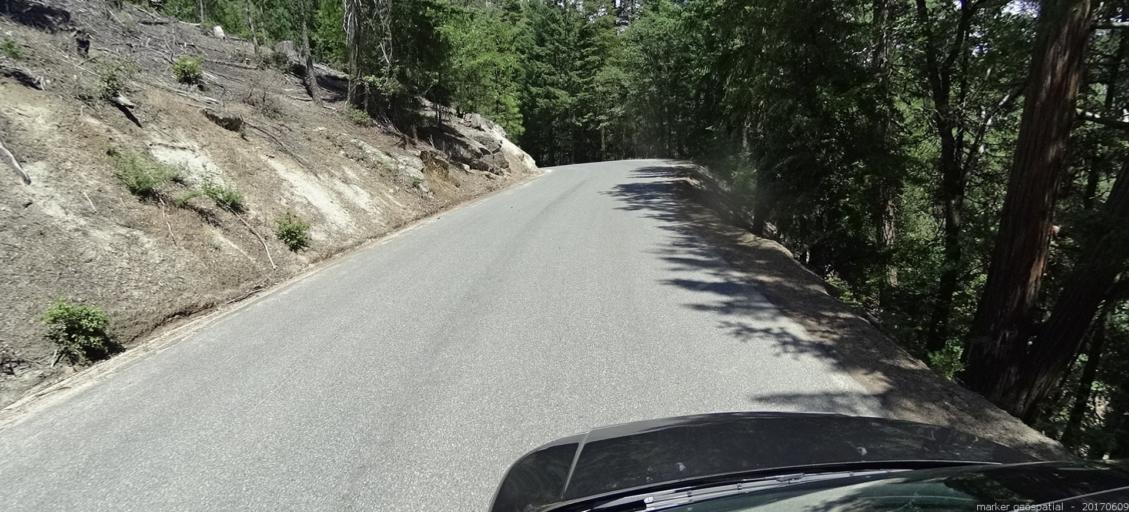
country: US
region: California
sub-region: Siskiyou County
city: Yreka
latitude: 41.4292
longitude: -122.9383
